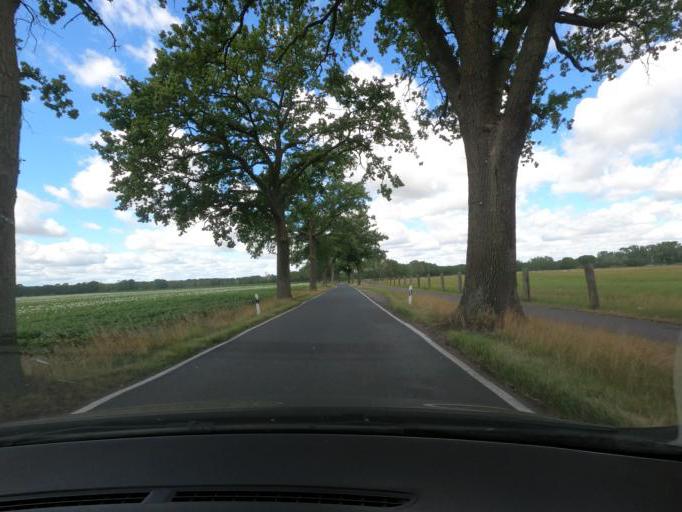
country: DE
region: Brandenburg
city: Kremmen
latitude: 52.7296
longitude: 12.9840
